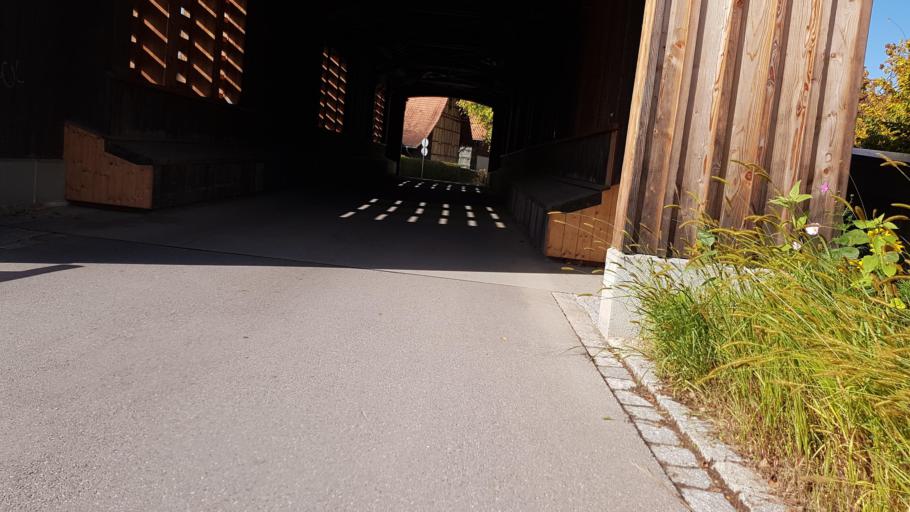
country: DE
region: Baden-Wuerttemberg
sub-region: Tuebingen Region
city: Eriskirch
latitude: 47.6284
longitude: 9.5323
